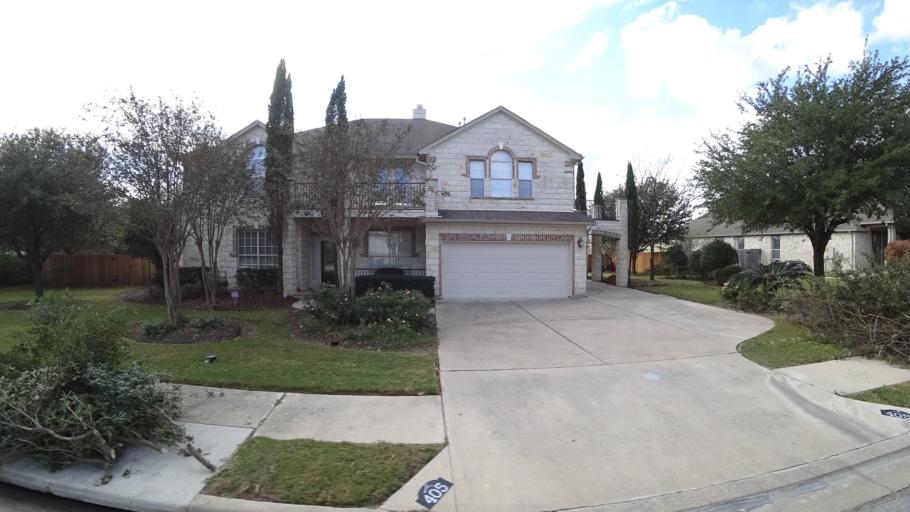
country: US
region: Texas
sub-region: Travis County
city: Pflugerville
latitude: 30.4287
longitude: -97.6309
